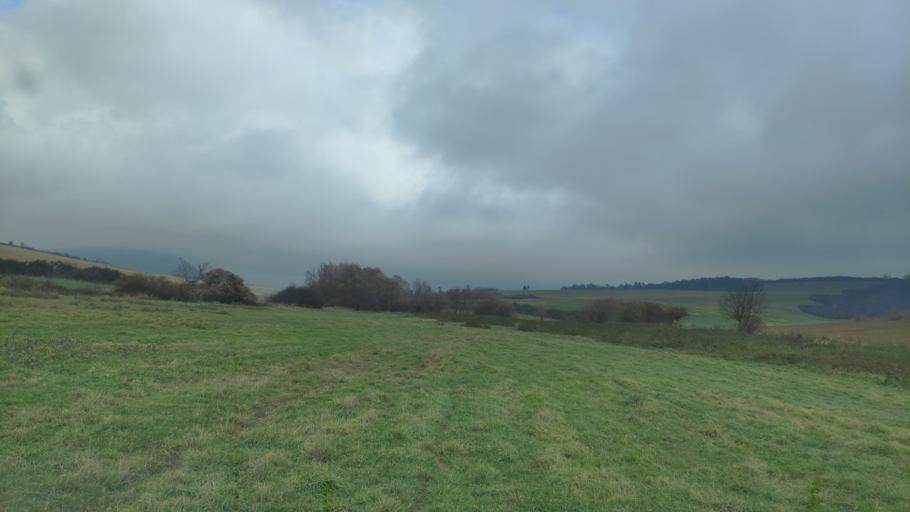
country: SK
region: Presovsky
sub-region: Okres Presov
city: Presov
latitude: 49.0157
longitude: 21.2002
